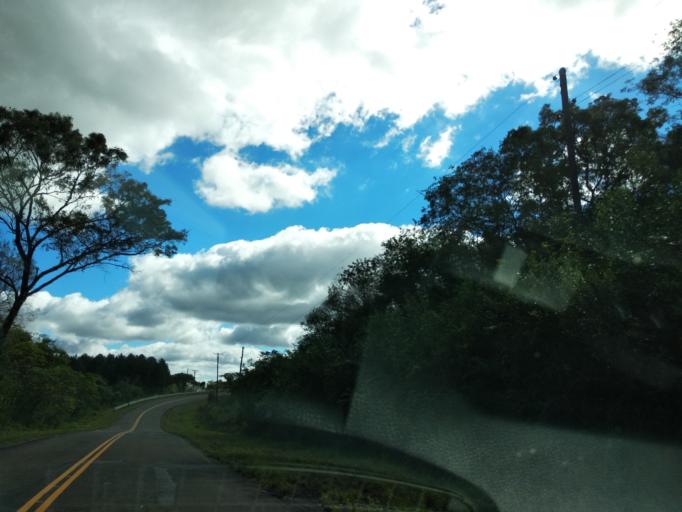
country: AR
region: Misiones
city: Santa Ana
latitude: -27.4200
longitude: -55.5690
